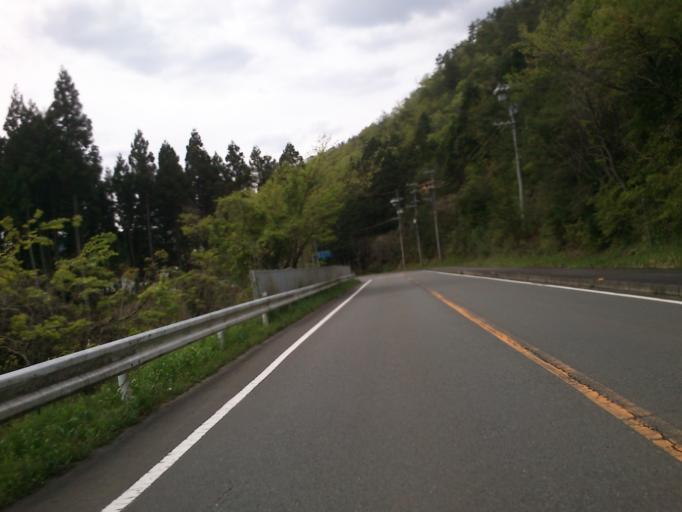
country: JP
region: Kyoto
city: Maizuru
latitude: 35.2822
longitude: 135.5334
